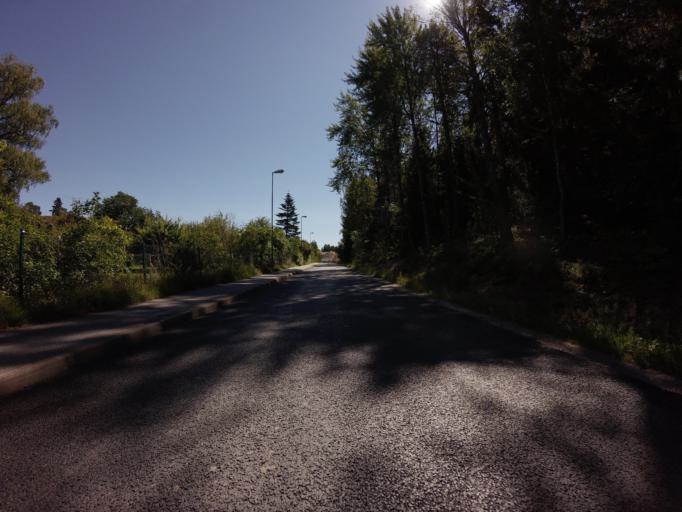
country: SE
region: Stockholm
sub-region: Jarfalla Kommun
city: Jakobsberg
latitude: 59.4631
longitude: 17.8822
